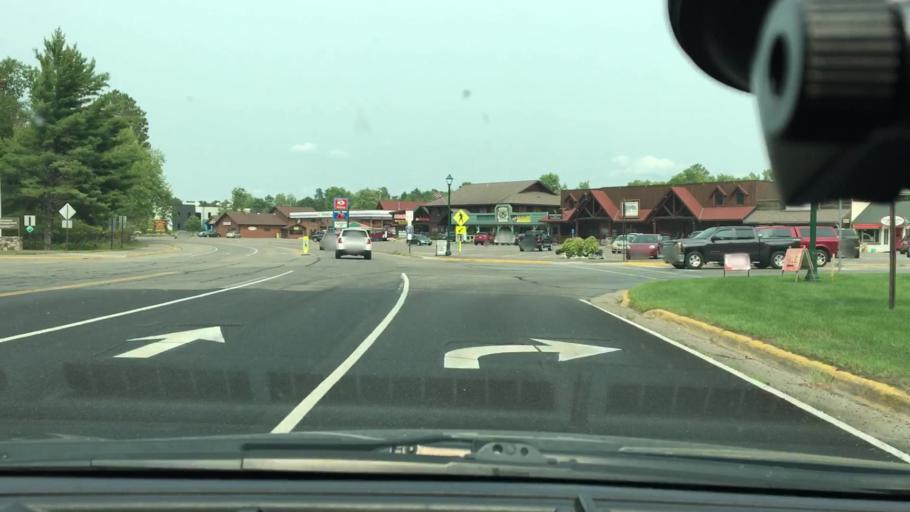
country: US
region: Minnesota
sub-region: Crow Wing County
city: Cross Lake
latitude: 46.6691
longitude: -94.1097
